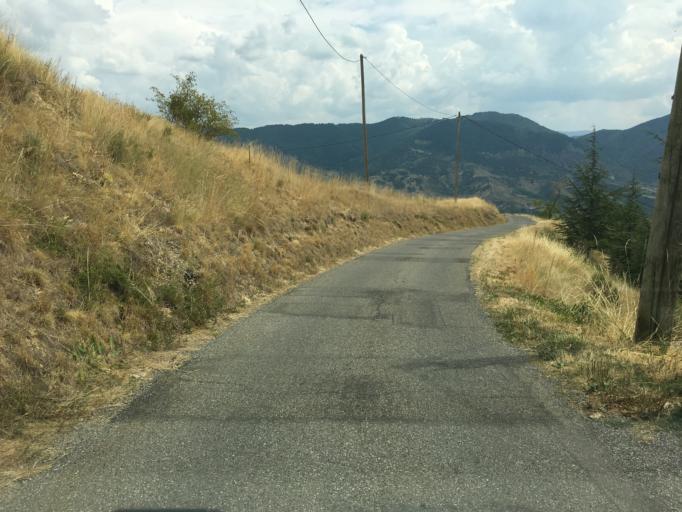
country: FR
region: Provence-Alpes-Cote d'Azur
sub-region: Departement des Alpes-de-Haute-Provence
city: Digne-les-Bains
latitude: 44.1970
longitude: 6.1363
